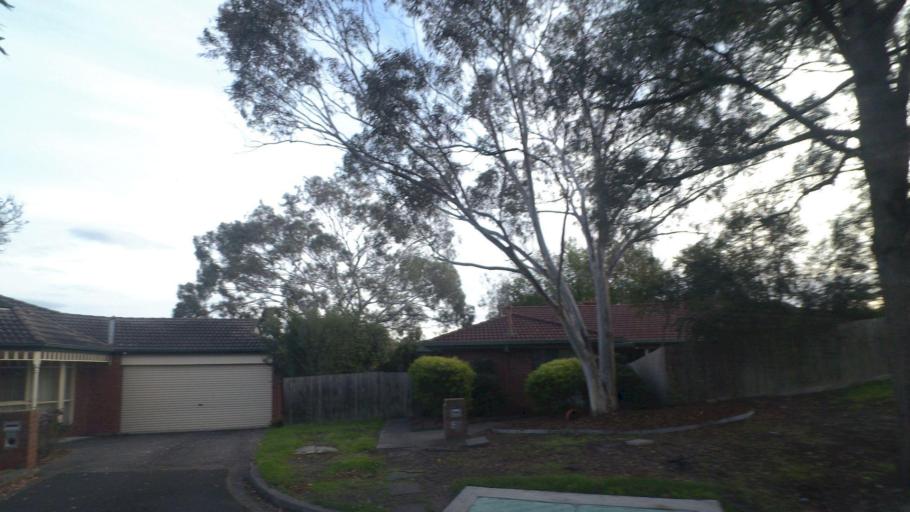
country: AU
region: Victoria
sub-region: Banyule
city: Yallambie
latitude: -37.7257
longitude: 145.1018
